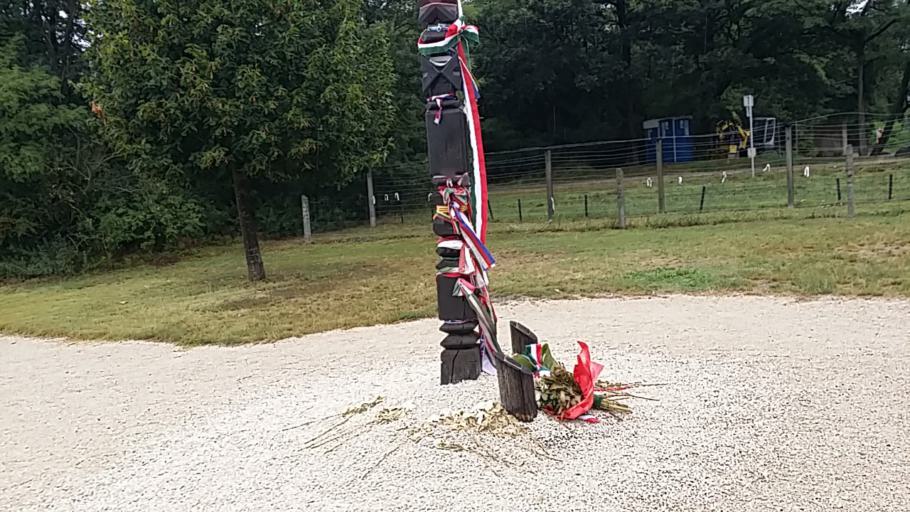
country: AT
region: Burgenland
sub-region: Eisenstadt-Umgebung
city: Morbisch am See
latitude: 47.7569
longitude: 16.6221
